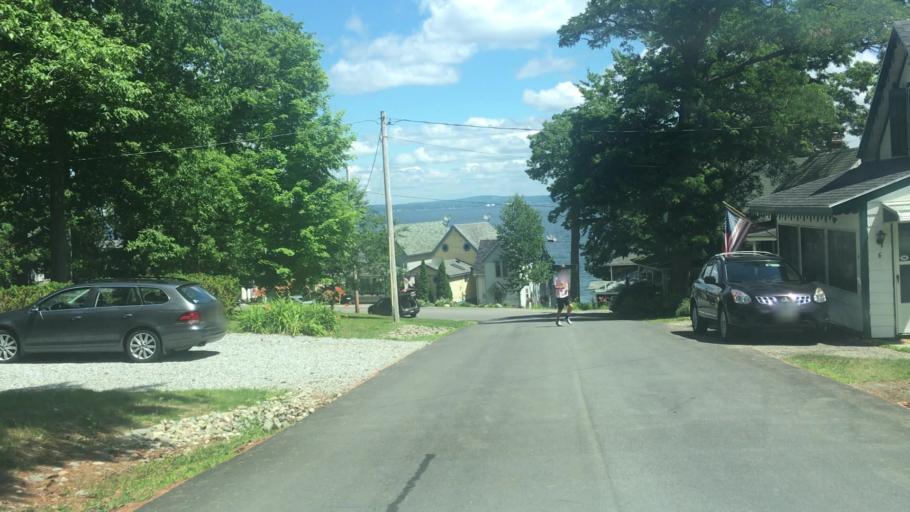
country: US
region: Maine
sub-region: Waldo County
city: Northport
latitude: 44.3790
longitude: -68.9677
